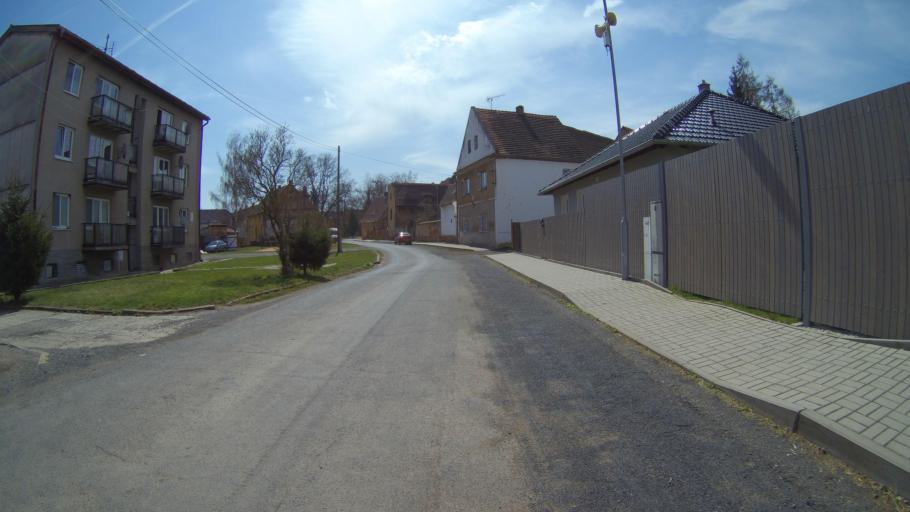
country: CZ
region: Ustecky
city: Kryry
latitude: 50.2004
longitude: 13.4611
